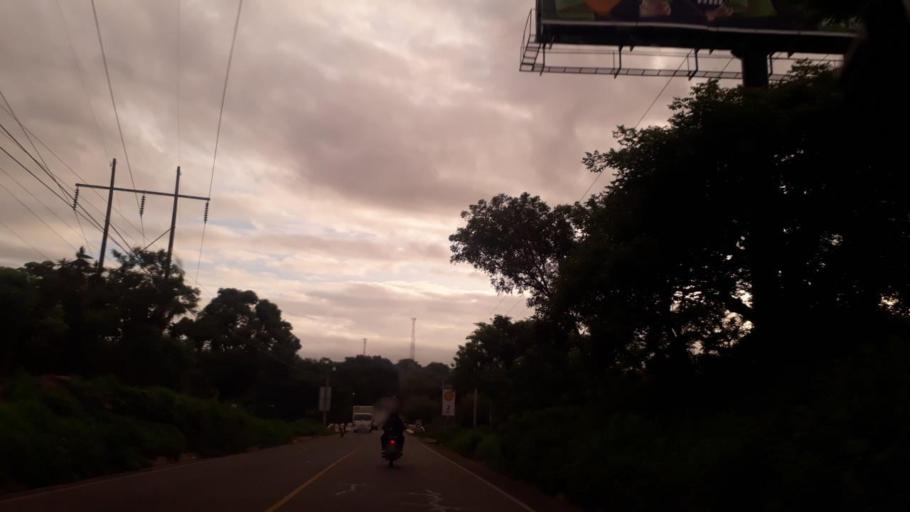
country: GT
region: Jutiapa
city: Jutiapa
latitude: 14.3136
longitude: -89.8666
